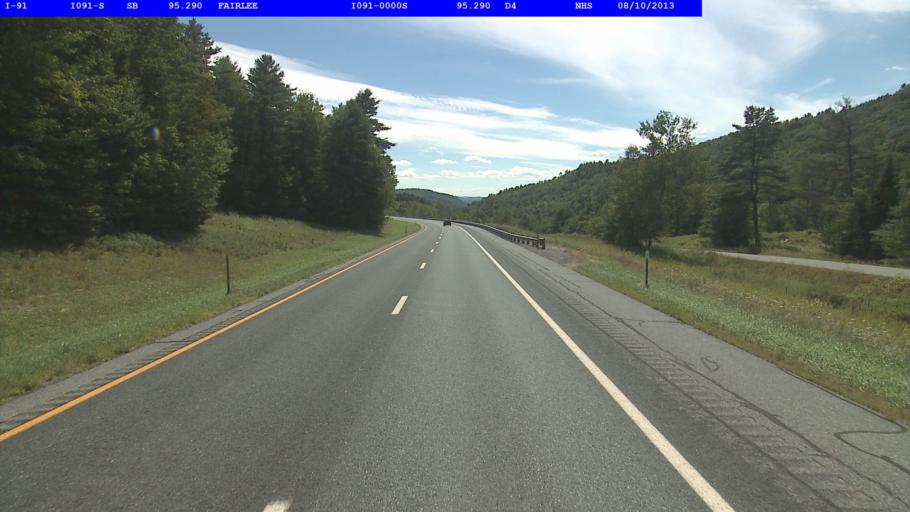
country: US
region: New Hampshire
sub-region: Grafton County
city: Orford
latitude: 43.9519
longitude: -72.1322
